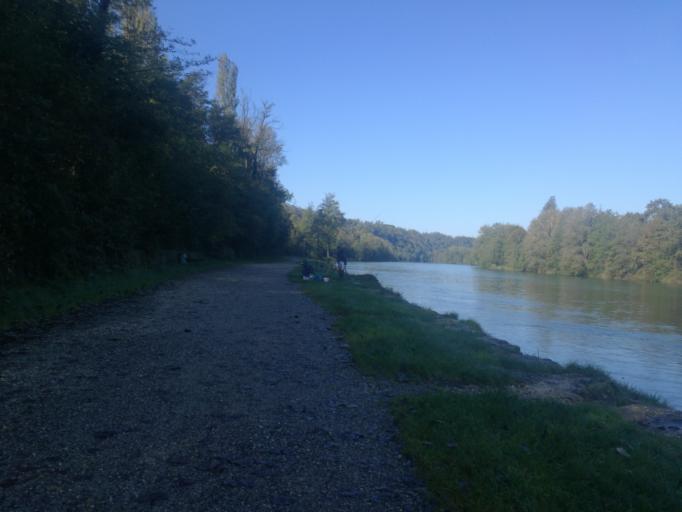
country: IT
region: Lombardy
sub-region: Provincia di Bergamo
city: Bottanuco
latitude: 45.6255
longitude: 9.5117
